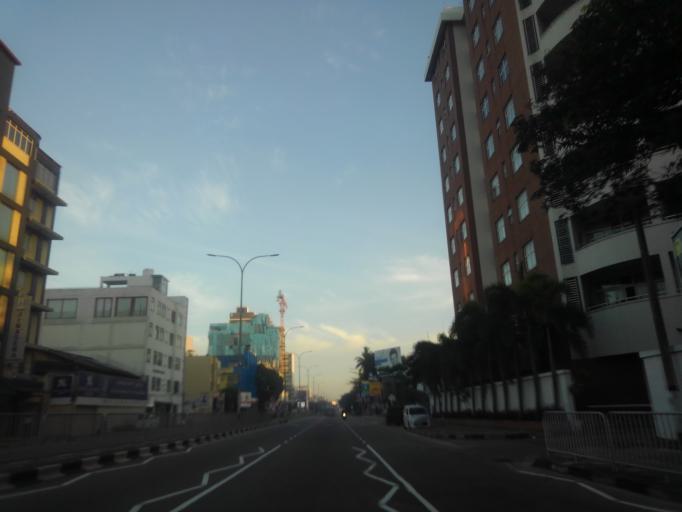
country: LK
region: Western
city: Pita Kotte
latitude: 6.9035
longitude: 79.8773
